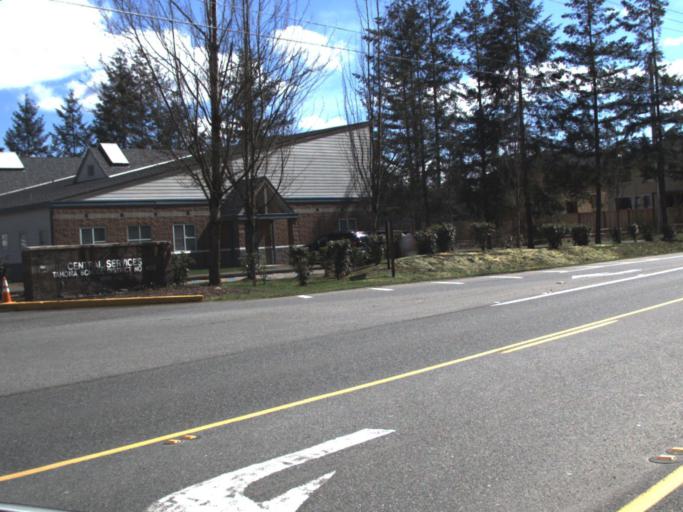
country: US
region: Washington
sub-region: King County
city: Maple Valley
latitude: 47.3712
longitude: -122.0231
